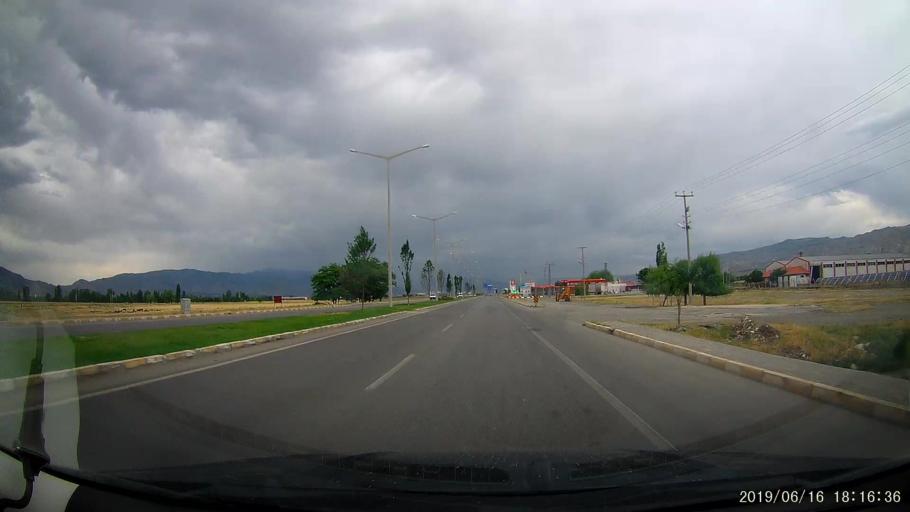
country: TR
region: Erzincan
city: Erzincan
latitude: 39.7293
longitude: 39.5457
